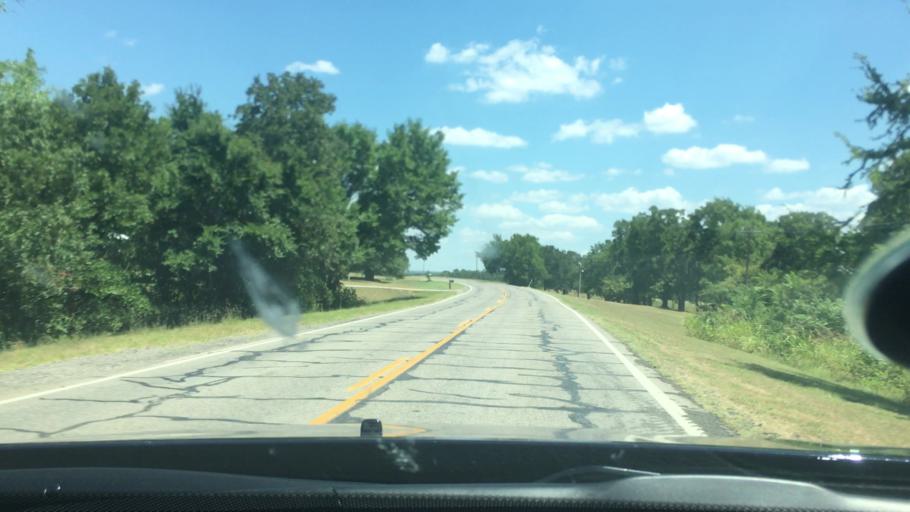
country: US
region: Oklahoma
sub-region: Carter County
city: Dickson
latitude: 34.2017
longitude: -96.9790
